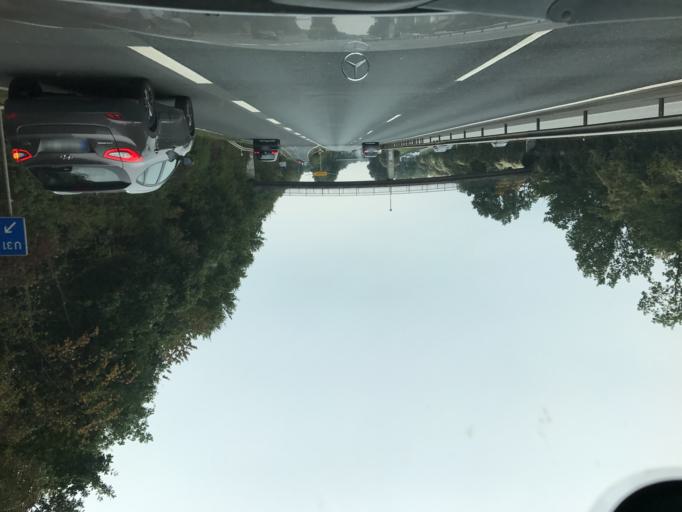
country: DE
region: Bremen
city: Bremen
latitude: 53.0380
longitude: 8.8466
